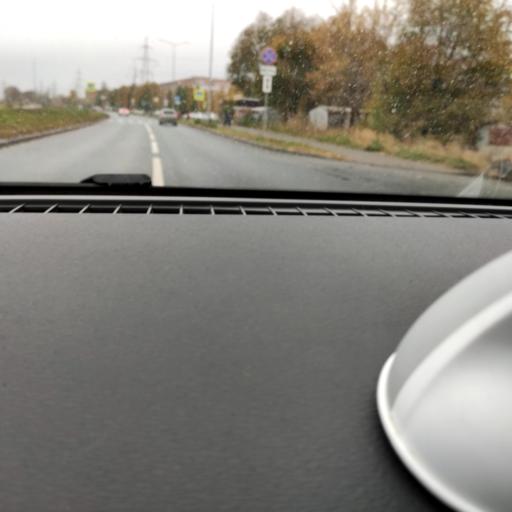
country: RU
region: Samara
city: Samara
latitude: 53.2548
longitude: 50.2469
